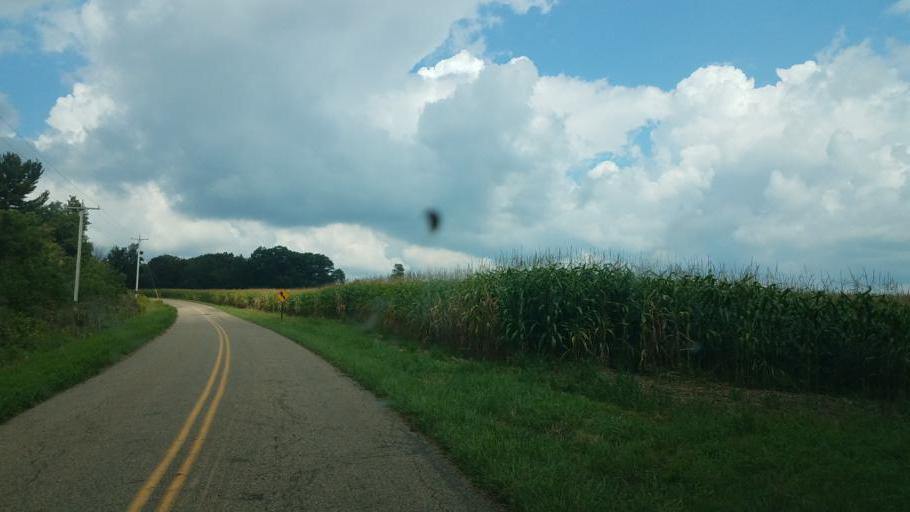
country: US
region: Ohio
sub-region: Licking County
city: Utica
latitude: 40.3063
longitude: -82.4870
